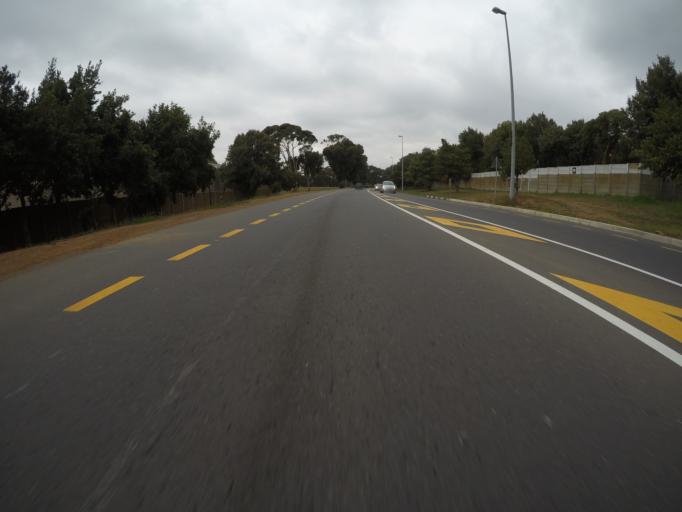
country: ZA
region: Western Cape
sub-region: City of Cape Town
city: Kraaifontein
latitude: -33.8430
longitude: 18.6368
